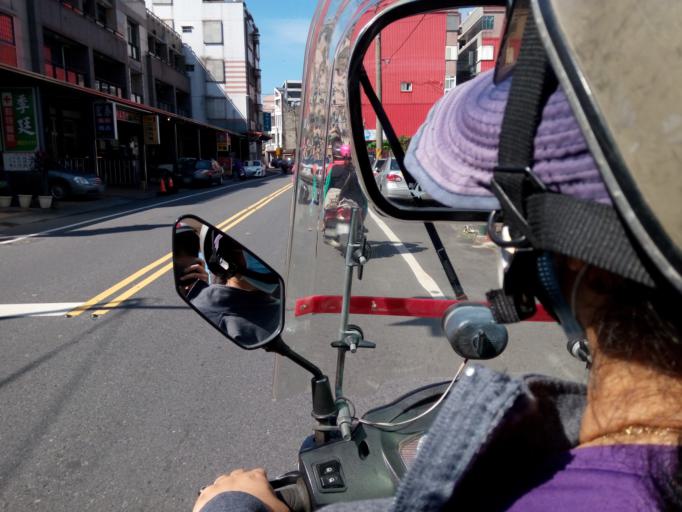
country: TW
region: Taiwan
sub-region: Yilan
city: Yilan
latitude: 24.6748
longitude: 121.7768
